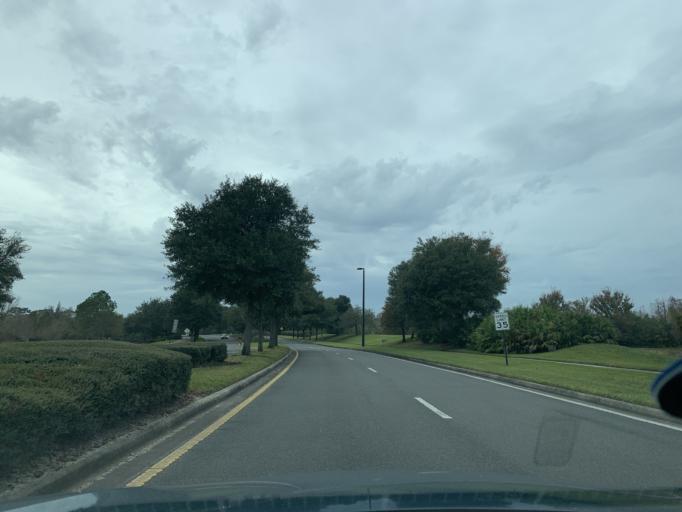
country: US
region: Florida
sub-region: Pasco County
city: Land O' Lakes
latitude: 28.2899
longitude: -82.4816
